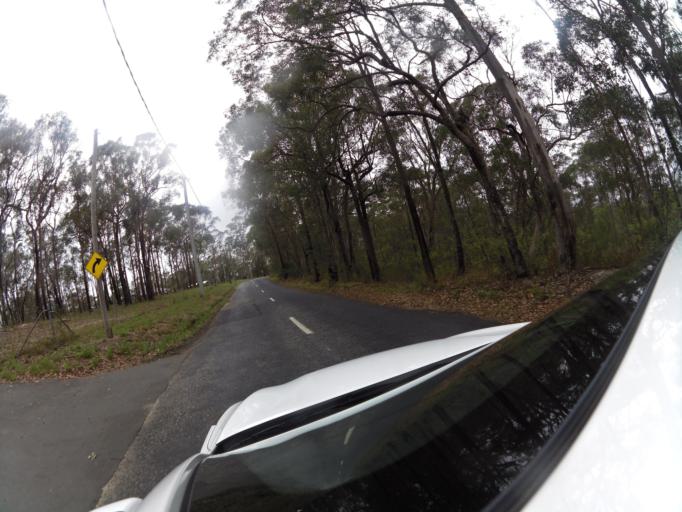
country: AU
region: New South Wales
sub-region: Hawkesbury
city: Pitt Town
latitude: -33.4433
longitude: 150.9284
